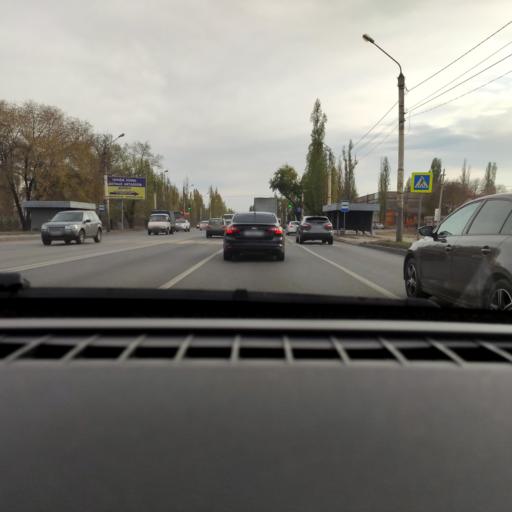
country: RU
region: Voronezj
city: Voronezh
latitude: 51.6273
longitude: 39.2308
